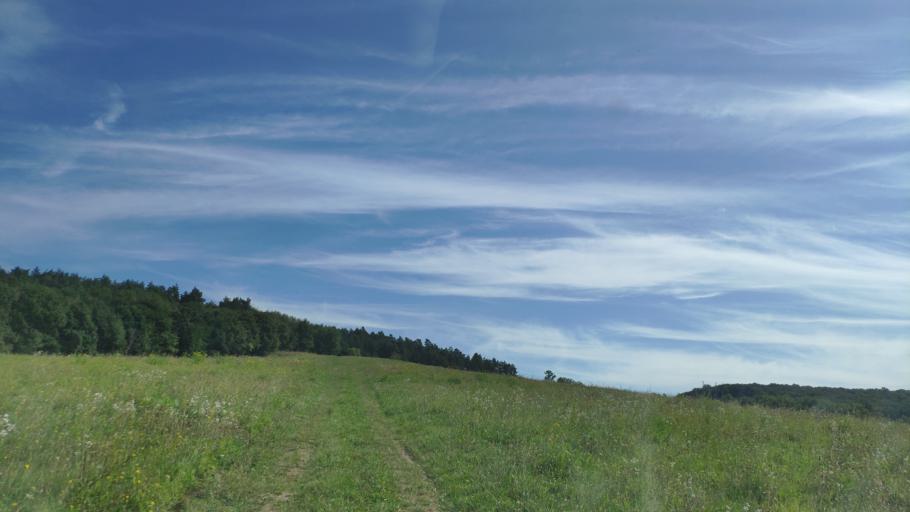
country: SK
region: Kosicky
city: Kosice
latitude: 48.8142
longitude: 21.3406
